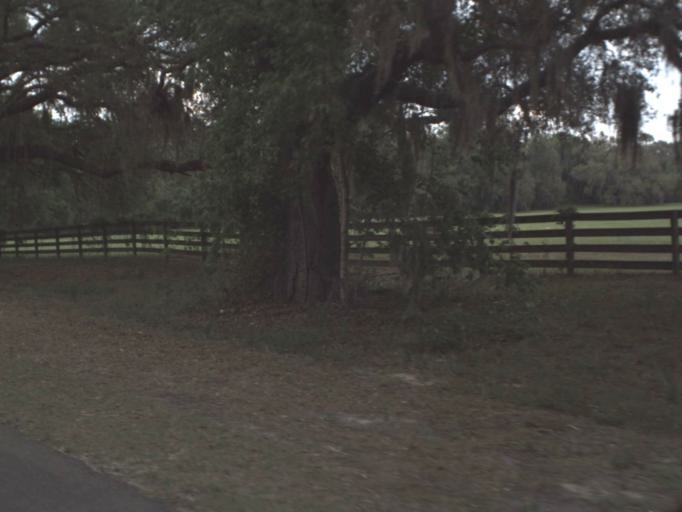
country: US
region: Florida
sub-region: Lake County
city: Umatilla
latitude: 28.9953
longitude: -81.6425
